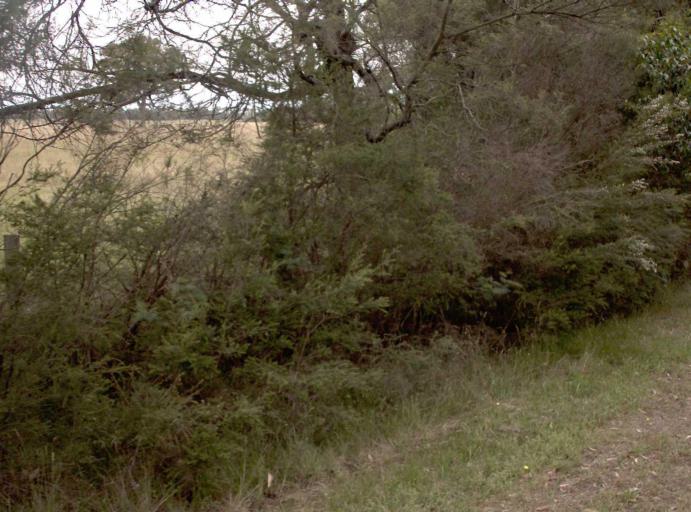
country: AU
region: Victoria
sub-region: Latrobe
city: Traralgon
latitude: -38.5025
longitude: 146.8353
